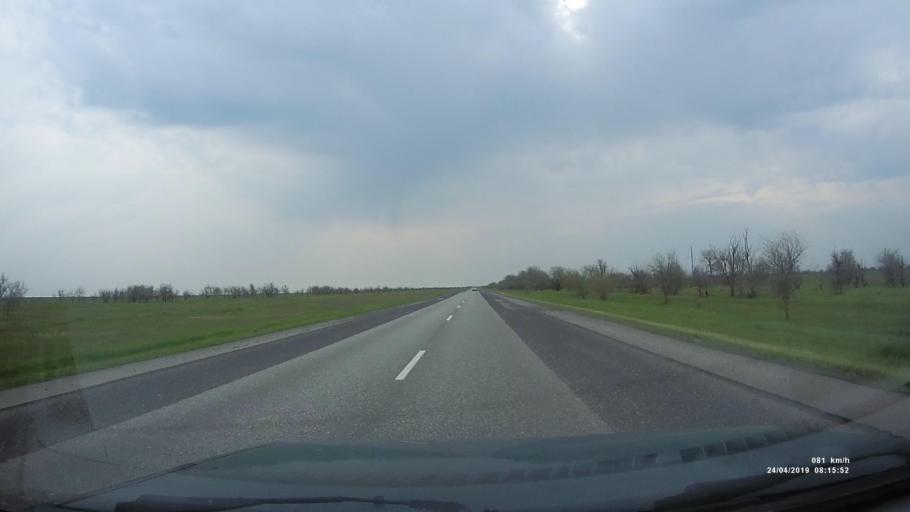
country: RU
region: Kalmykiya
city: Priyutnoye
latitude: 46.0996
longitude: 43.6020
